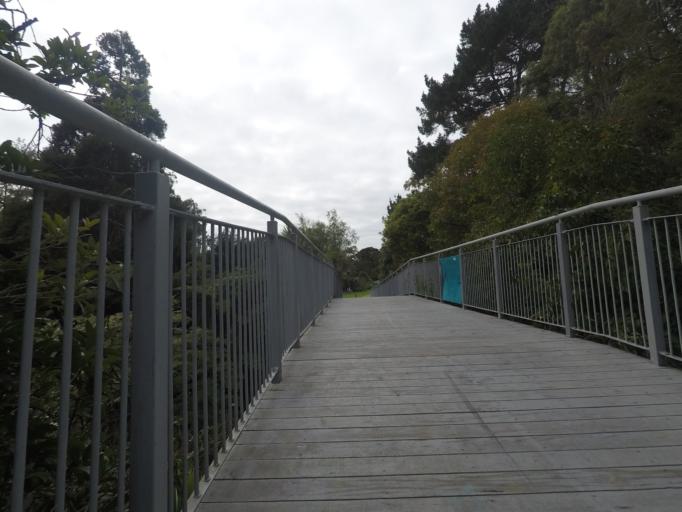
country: NZ
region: Auckland
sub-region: Auckland
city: Waitakere
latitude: -36.8942
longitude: 174.6325
